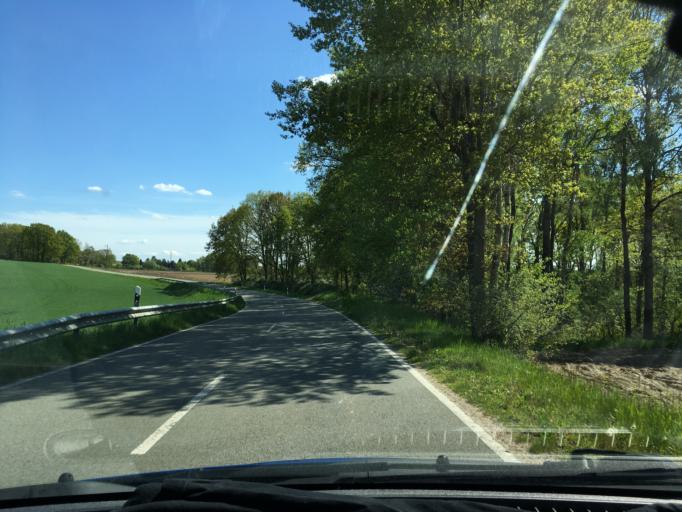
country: DE
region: Lower Saxony
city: Zernien
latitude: 53.0390
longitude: 10.8808
